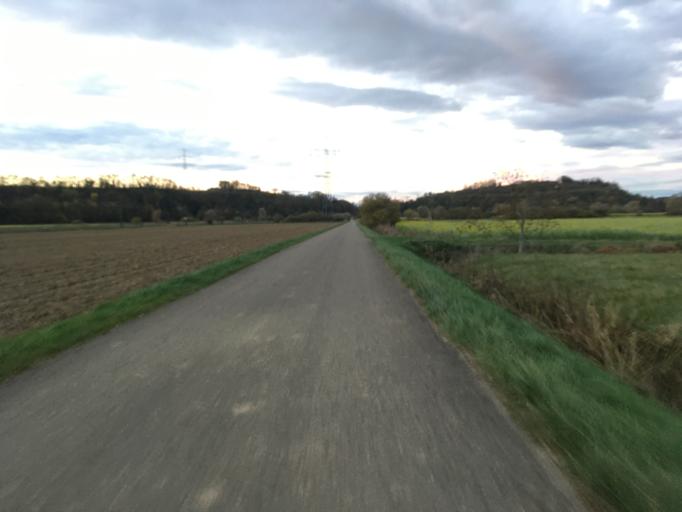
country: DE
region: Baden-Wuerttemberg
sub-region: Freiburg Region
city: Bahlingen
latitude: 48.1348
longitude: 7.7438
